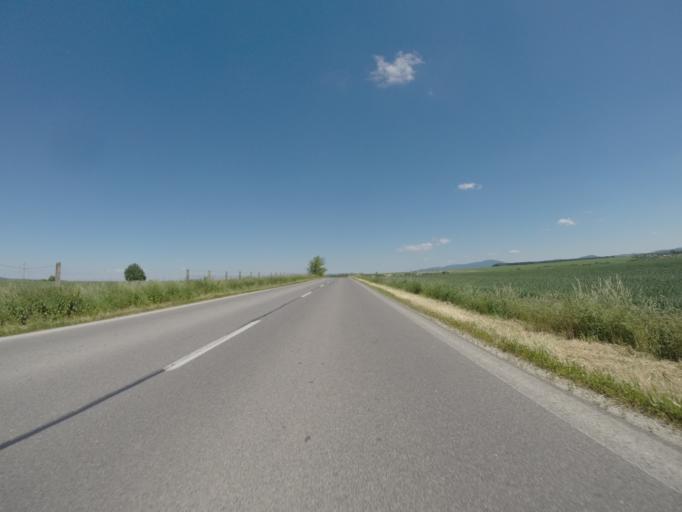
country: SK
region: Trnavsky
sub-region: Okres Trnava
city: Piestany
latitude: 48.5148
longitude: 17.9990
